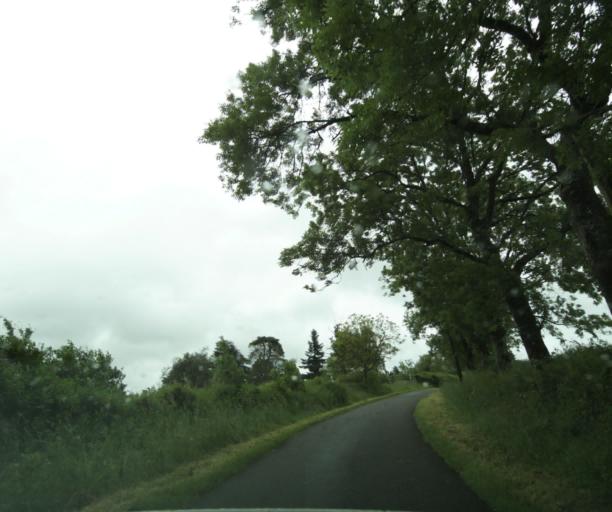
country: FR
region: Bourgogne
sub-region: Departement de Saone-et-Loire
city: Saint-Vallier
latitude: 46.4946
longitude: 4.4577
